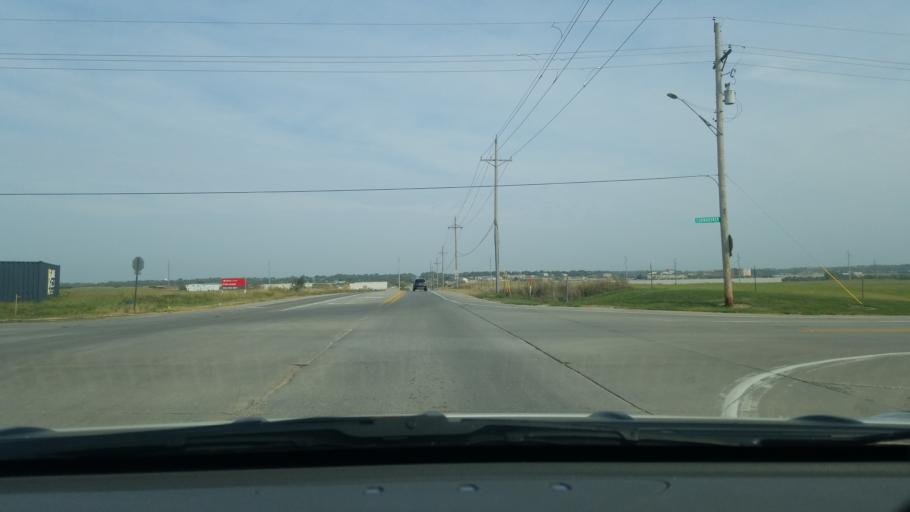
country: US
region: Nebraska
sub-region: Sarpy County
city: Chalco
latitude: 41.1623
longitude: -96.1196
